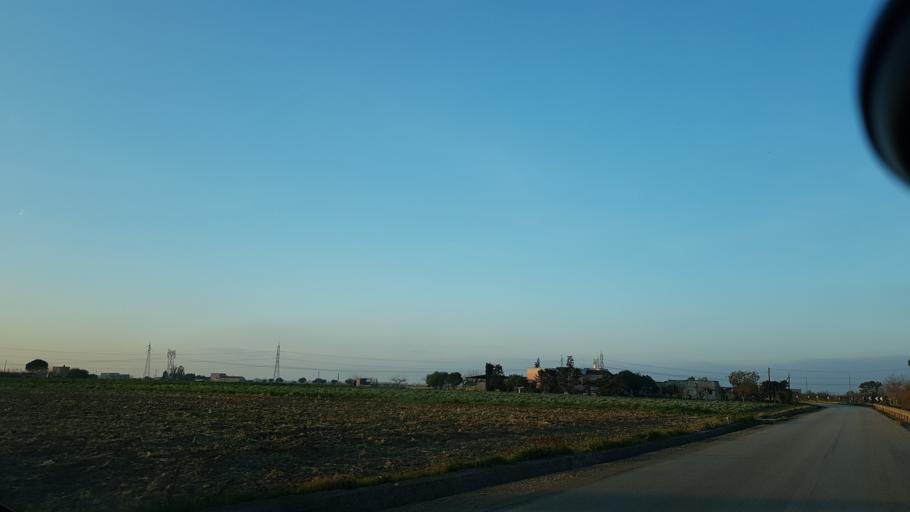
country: IT
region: Apulia
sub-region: Provincia di Brindisi
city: La Rosa
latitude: 40.5953
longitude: 17.9461
